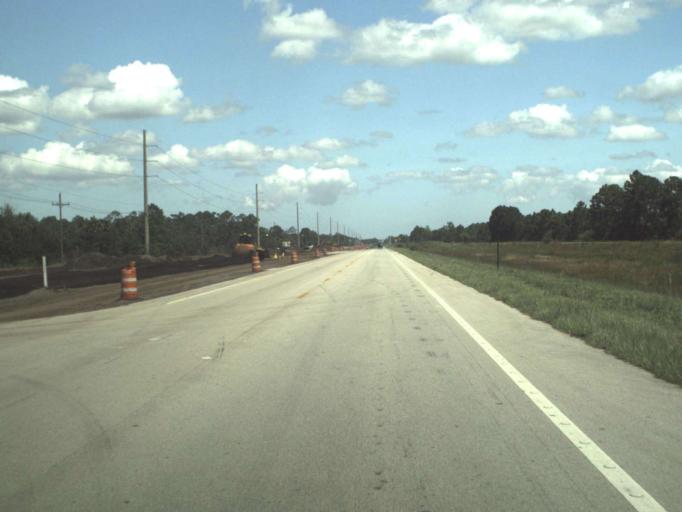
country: US
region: Florida
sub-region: Palm Beach County
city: Limestone Creek
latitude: 26.9172
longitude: -80.3132
